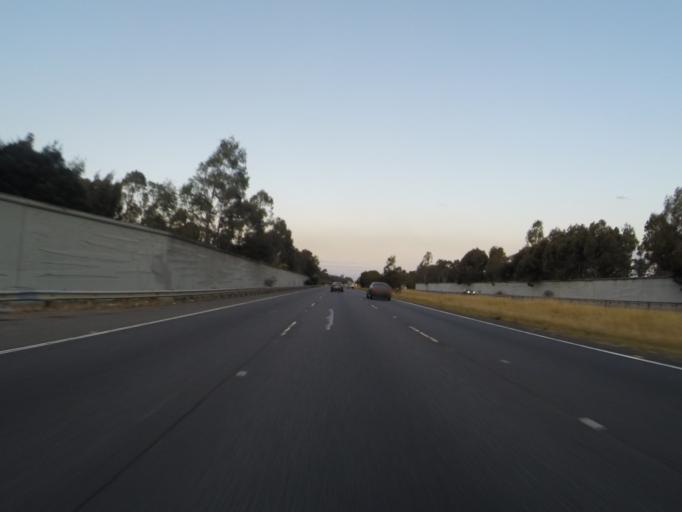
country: AU
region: New South Wales
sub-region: Blacktown
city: Mount Druitt
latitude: -33.7850
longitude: 150.7777
